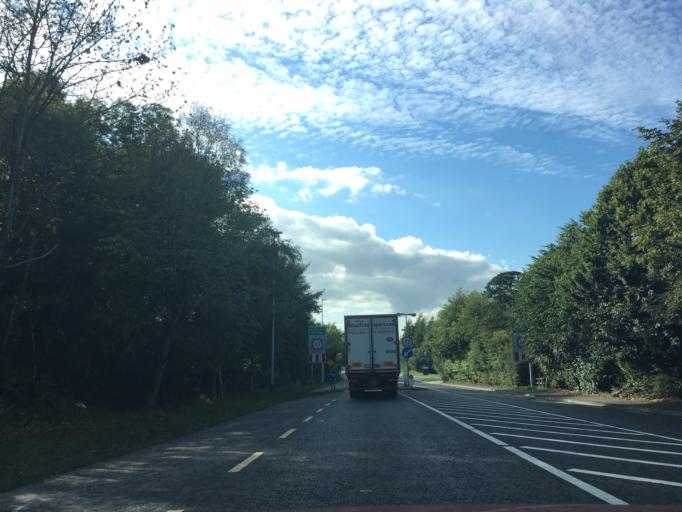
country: IE
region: Leinster
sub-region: Loch Garman
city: New Ross
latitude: 52.3848
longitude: -6.9476
